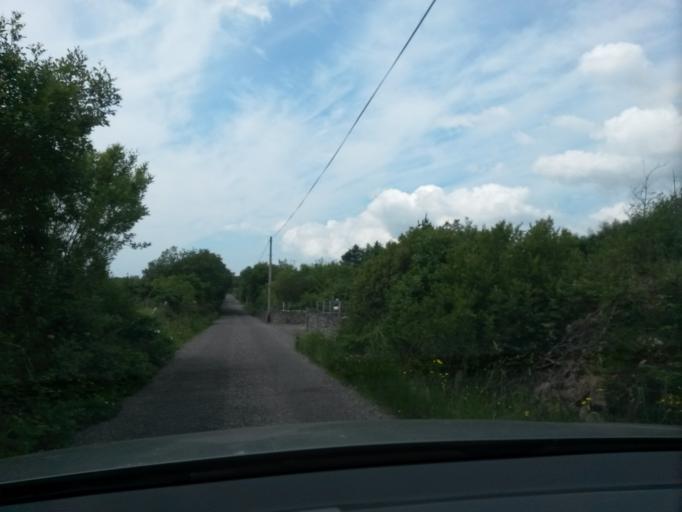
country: IE
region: Munster
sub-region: Ciarrai
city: Cahersiveen
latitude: 51.7998
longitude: -9.9530
